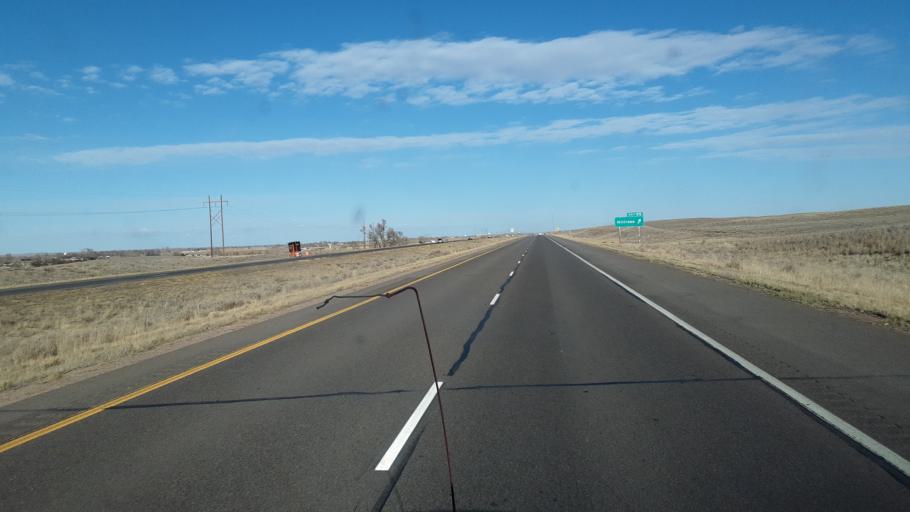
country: US
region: Colorado
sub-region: Morgan County
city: Brush
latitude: 40.2968
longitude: -103.5349
